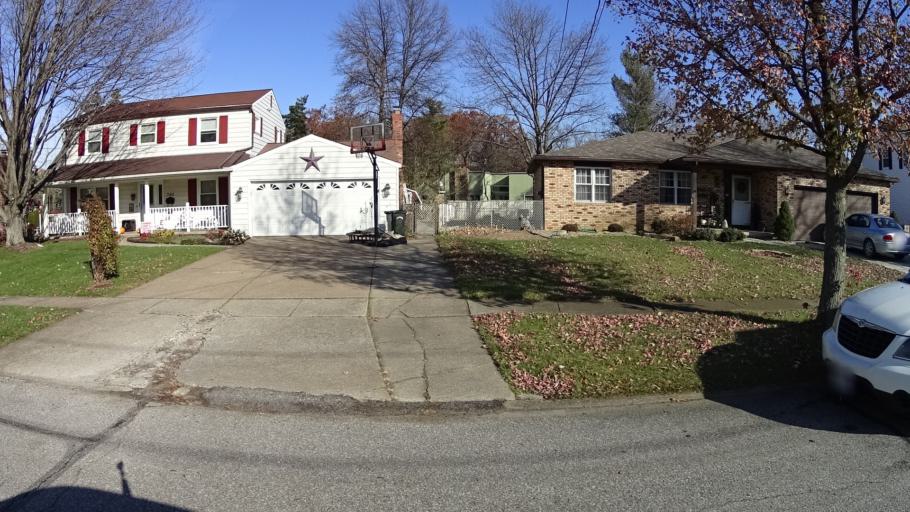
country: US
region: Ohio
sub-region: Lorain County
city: Sheffield
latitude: 41.4039
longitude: -82.0819
